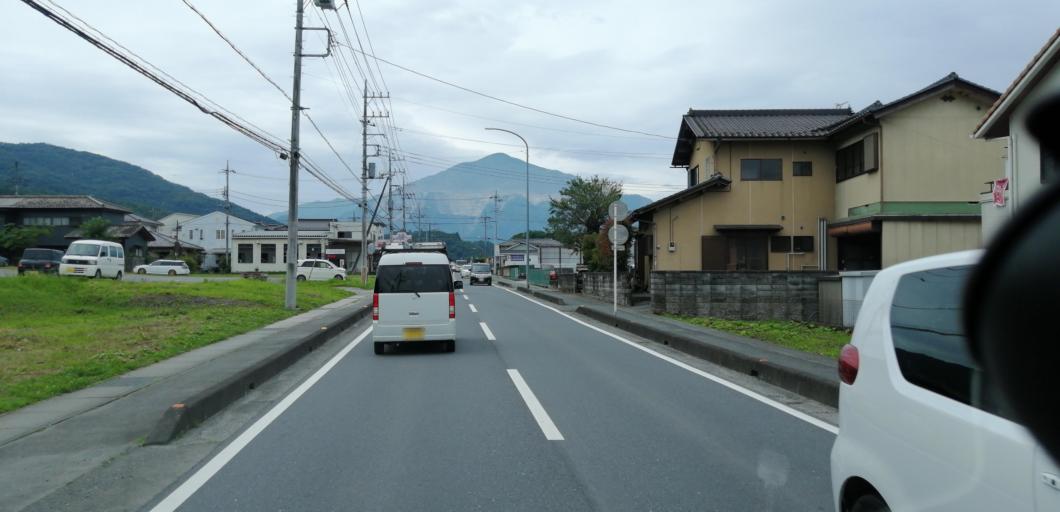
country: JP
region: Saitama
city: Chichibu
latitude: 36.0165
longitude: 139.1126
